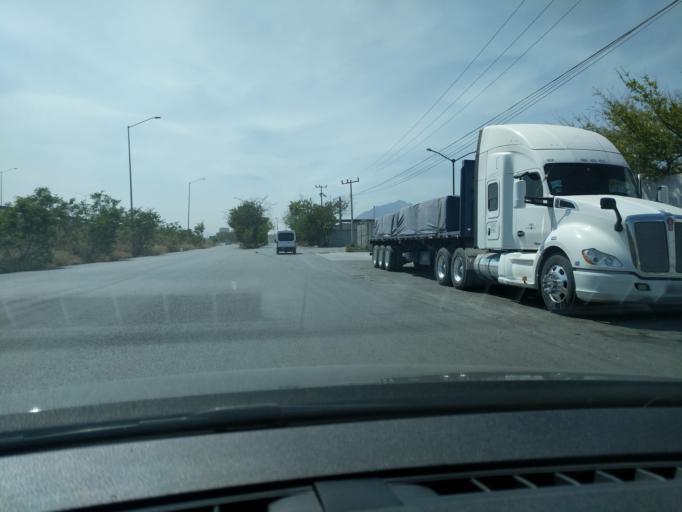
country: MX
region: Nuevo Leon
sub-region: Salinas Victoria
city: Simeprodeso (Colectivo Nuevo)
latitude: 25.8337
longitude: -100.3110
